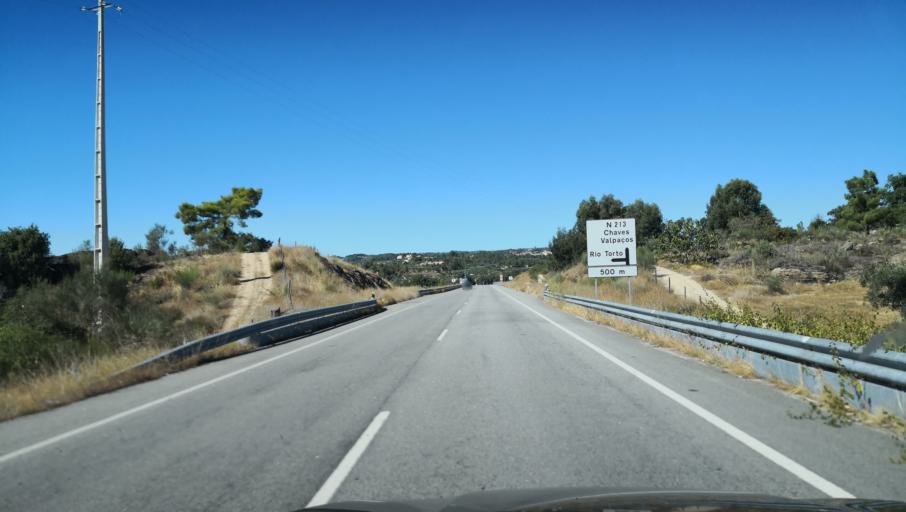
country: PT
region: Vila Real
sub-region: Valpacos
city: Valpacos
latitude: 41.5786
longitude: -7.3037
